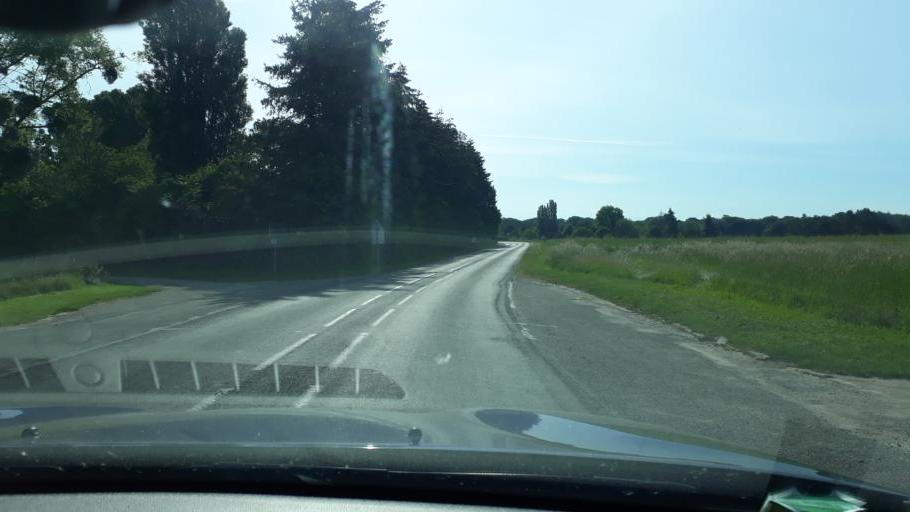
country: FR
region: Centre
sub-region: Departement du Loiret
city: Chilleurs-aux-Bois
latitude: 48.0656
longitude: 2.2170
